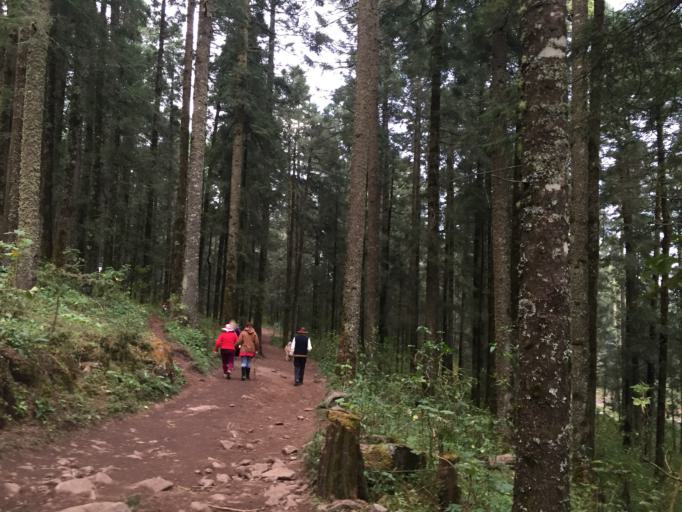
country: MX
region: Michoacan
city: Mineral de Angangueo
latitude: 19.6685
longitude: -100.2883
